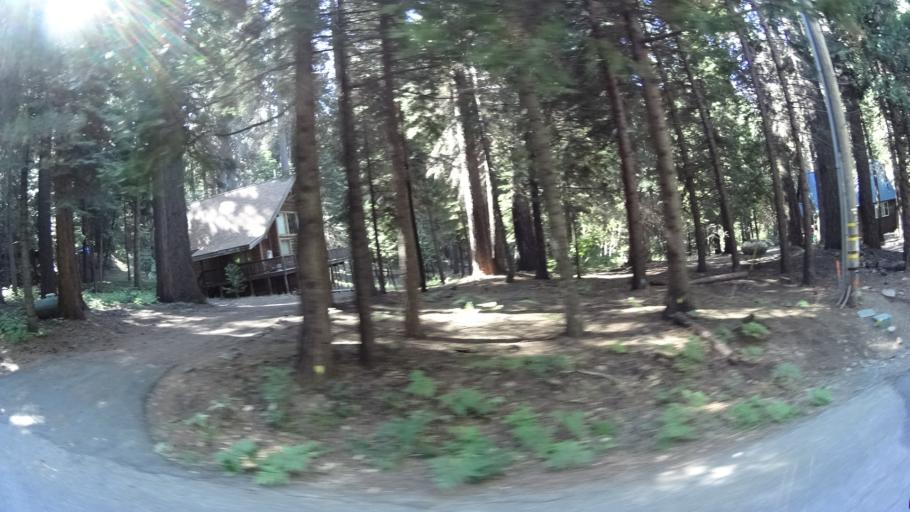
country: US
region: California
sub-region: Calaveras County
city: Arnold
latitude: 38.2948
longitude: -120.2736
